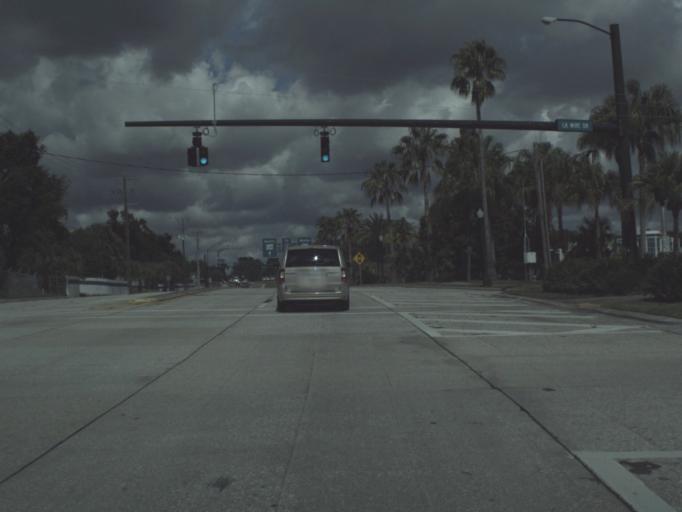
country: US
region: Florida
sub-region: Polk County
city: Lakeland
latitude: 28.0449
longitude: -81.9613
